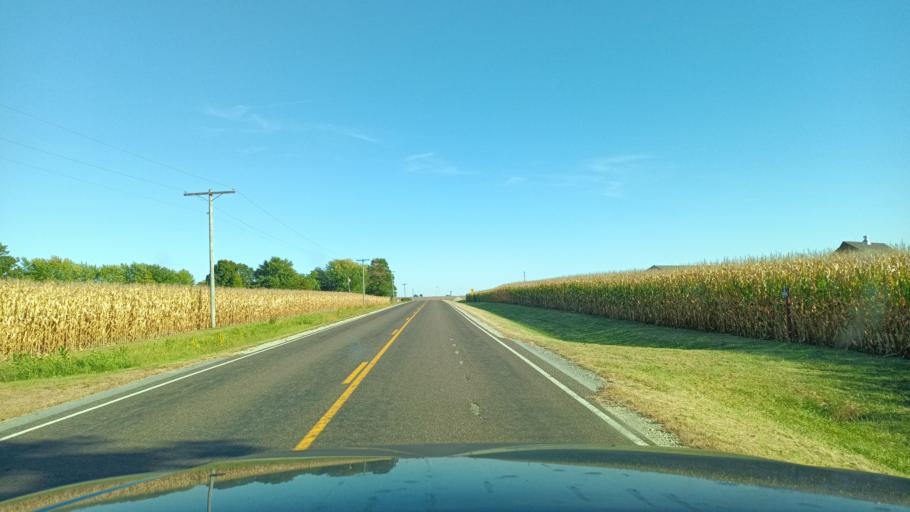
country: US
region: Illinois
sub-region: McLean County
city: Heyworth
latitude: 40.2354
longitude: -89.0742
